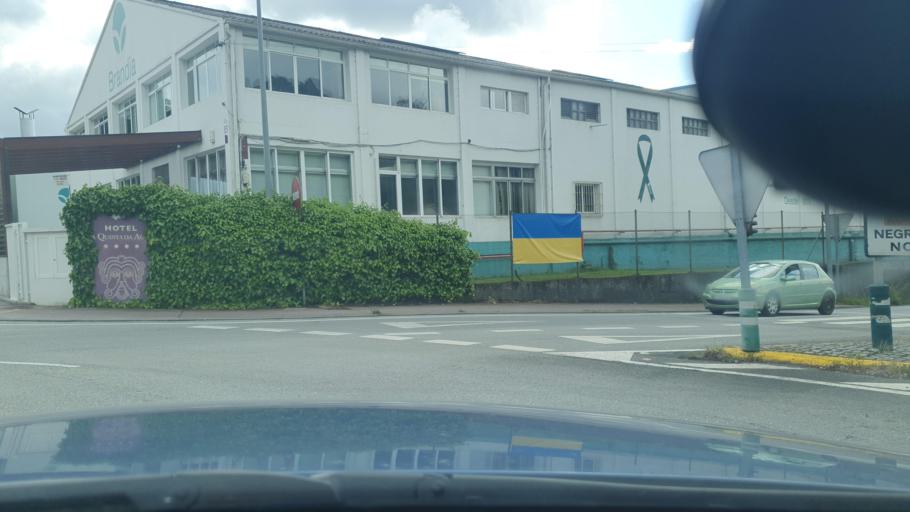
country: ES
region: Galicia
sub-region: Provincia da Coruna
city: Santiago de Compostela
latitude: 42.8726
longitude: -8.5803
